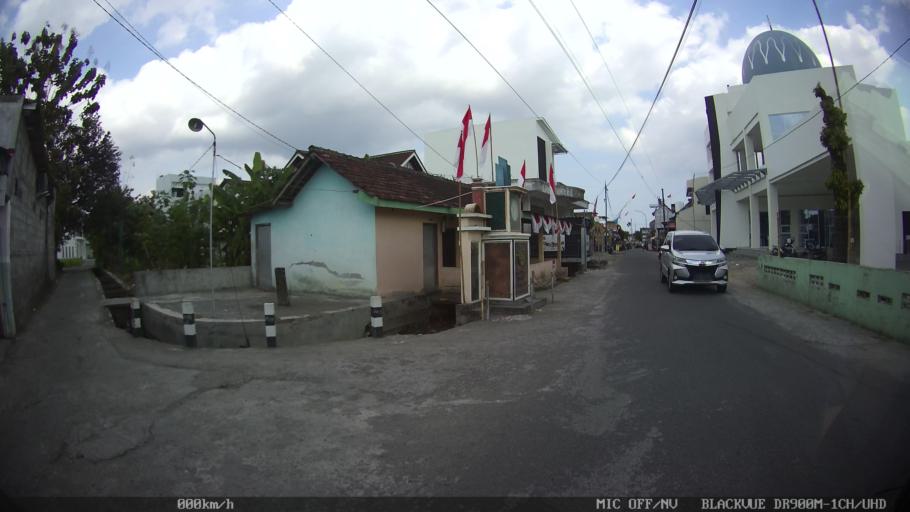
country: ID
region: Daerah Istimewa Yogyakarta
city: Kasihan
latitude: -7.8118
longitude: 110.3281
